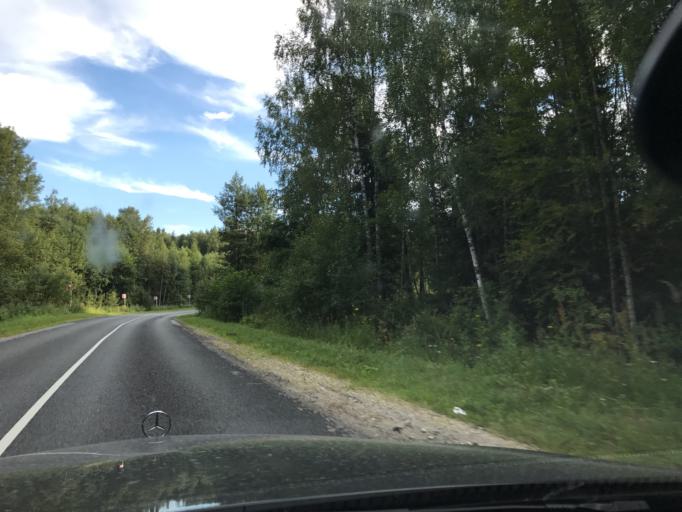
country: RU
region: Vladimir
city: Raduzhnyy
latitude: 55.9911
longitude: 40.2728
